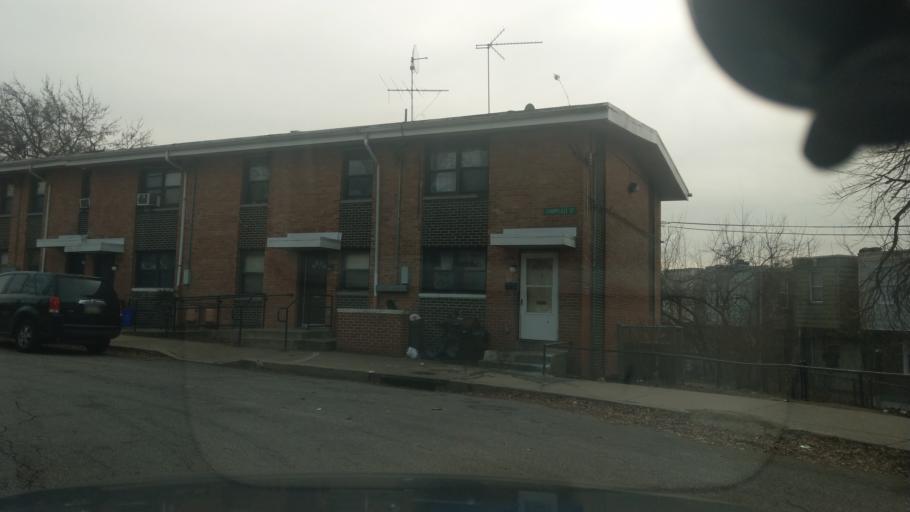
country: US
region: Pennsylvania
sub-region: Montgomery County
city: Wyncote
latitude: 40.0454
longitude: -75.1550
